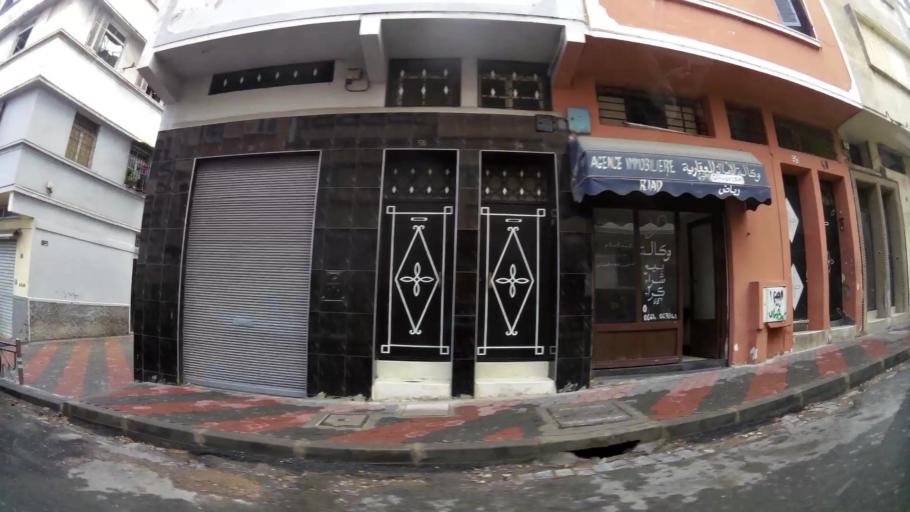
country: MA
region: Grand Casablanca
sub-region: Casablanca
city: Casablanca
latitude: 33.5633
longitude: -7.6112
